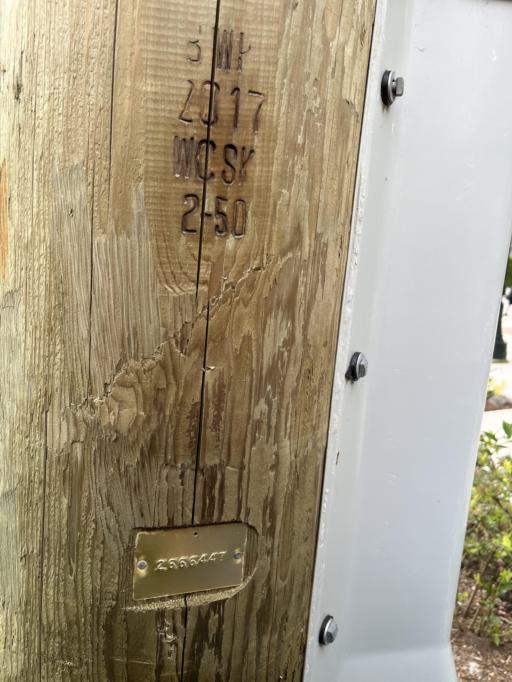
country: CA
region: British Columbia
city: Ladner
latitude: 49.0895
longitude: -123.0826
